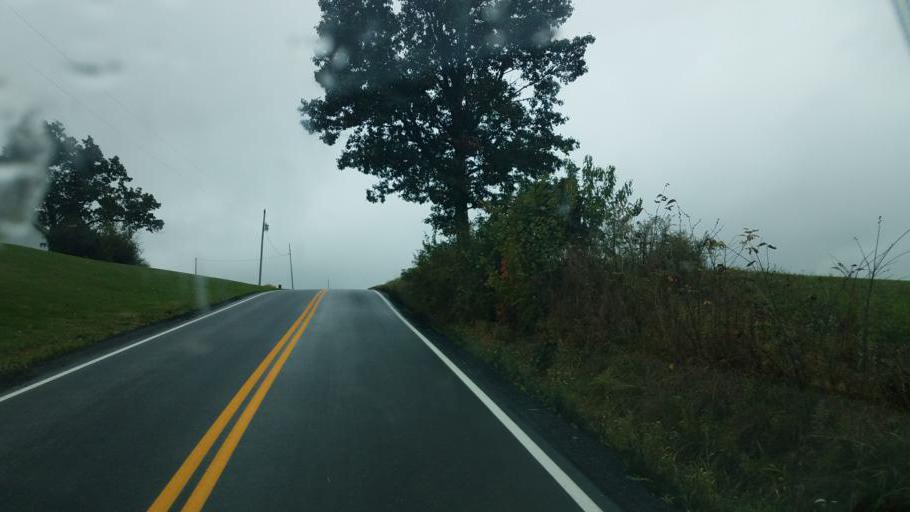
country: US
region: Ohio
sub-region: Wayne County
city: Shreve
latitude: 40.5933
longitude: -82.0628
